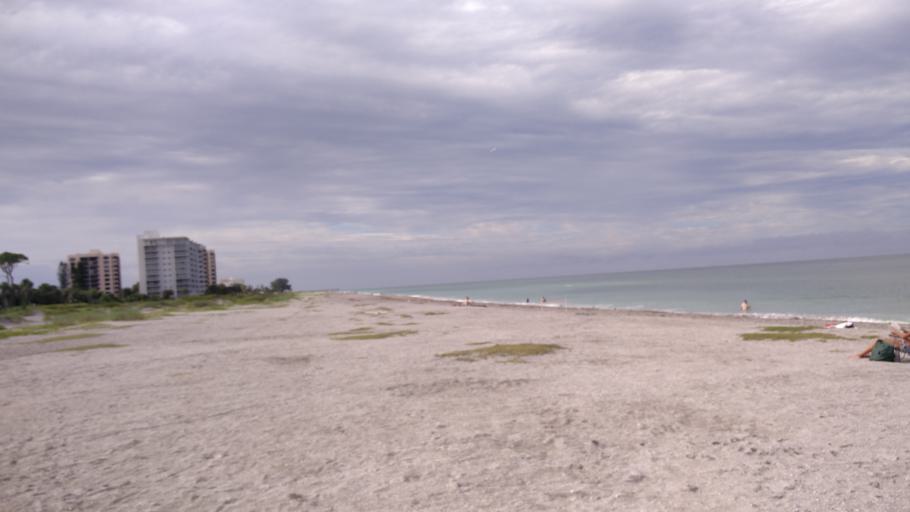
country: US
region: Florida
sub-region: Sarasota County
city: Venice
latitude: 27.0988
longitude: -82.4604
